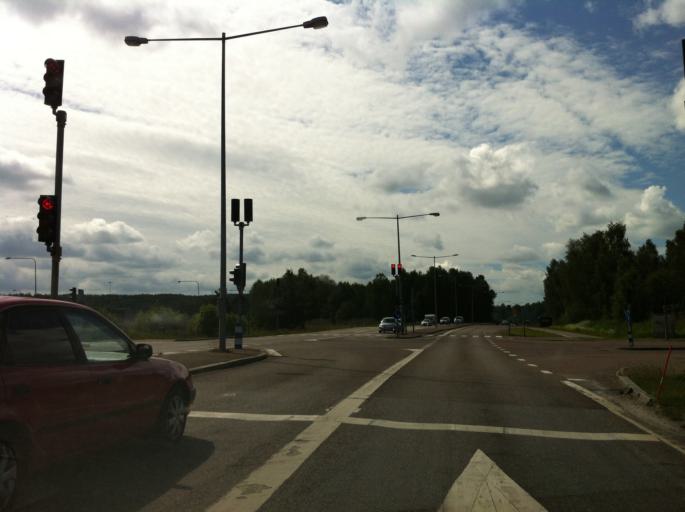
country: SE
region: Vaermland
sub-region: Grums Kommun
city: Grums
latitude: 59.3417
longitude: 13.1096
